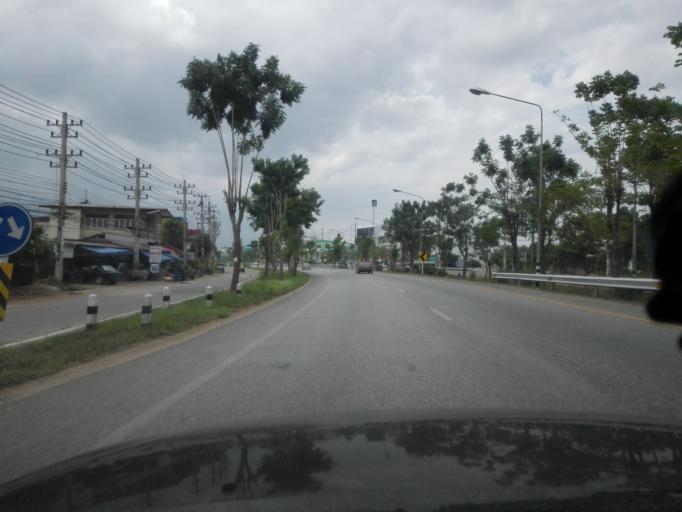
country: TH
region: Kamphaeng Phet
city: Kamphaeng Phet
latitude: 16.4780
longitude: 99.4964
